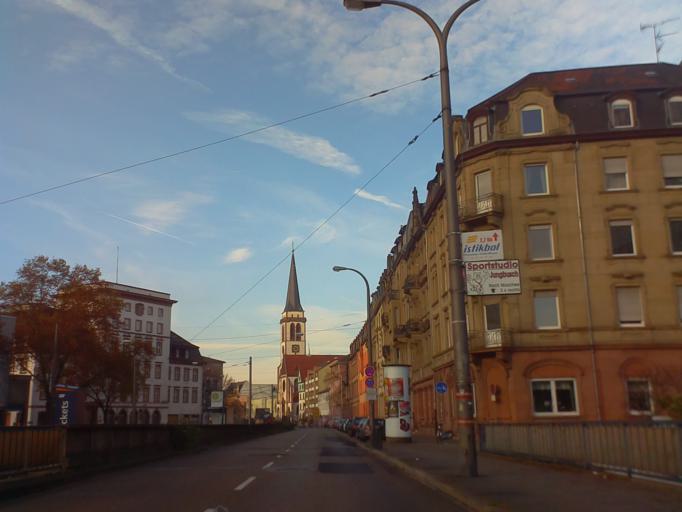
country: DE
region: Baden-Wuerttemberg
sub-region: Karlsruhe Region
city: Mannheim
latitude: 49.4940
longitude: 8.4665
